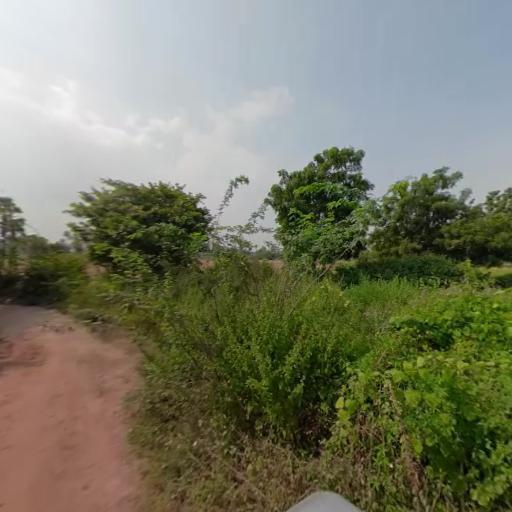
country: IN
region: Telangana
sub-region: Nalgonda
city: Suriapet
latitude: 17.2066
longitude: 79.4904
